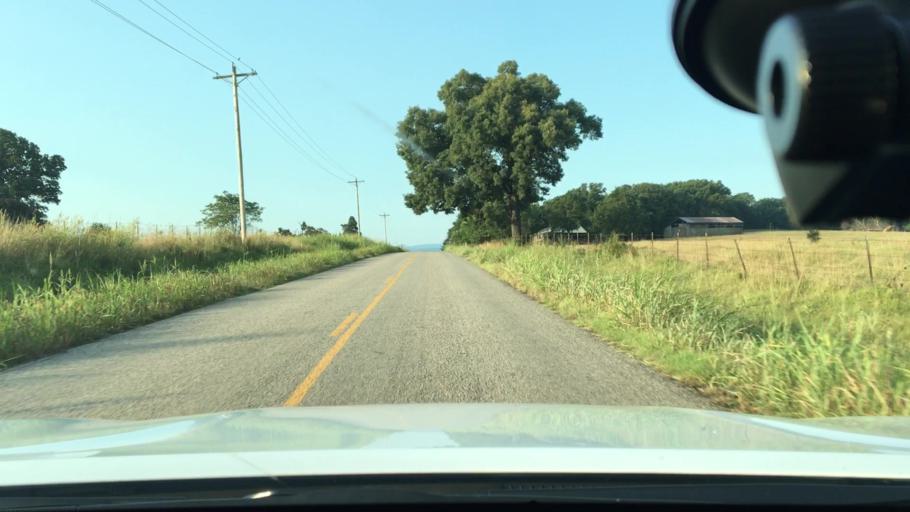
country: US
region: Arkansas
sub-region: Johnson County
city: Coal Hill
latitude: 35.3525
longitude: -93.6133
